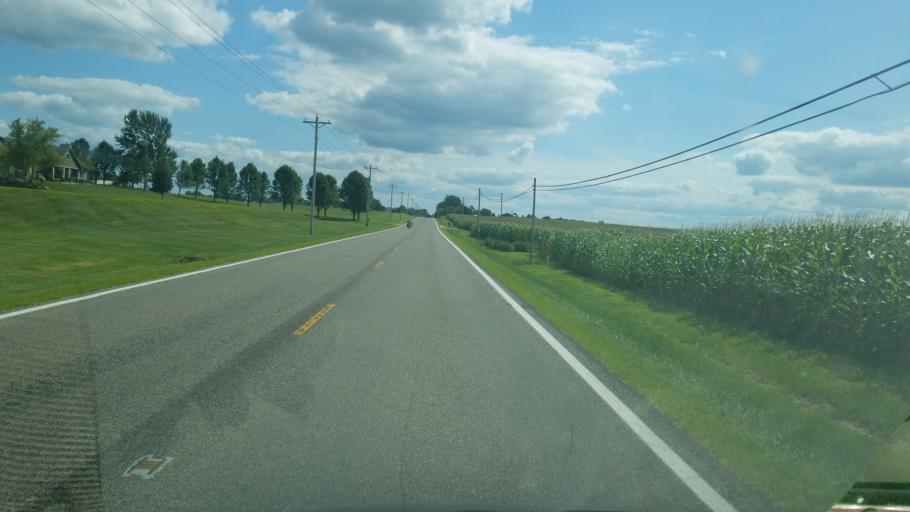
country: US
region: Ohio
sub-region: Logan County
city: Lakeview
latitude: 40.6259
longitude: -83.9755
